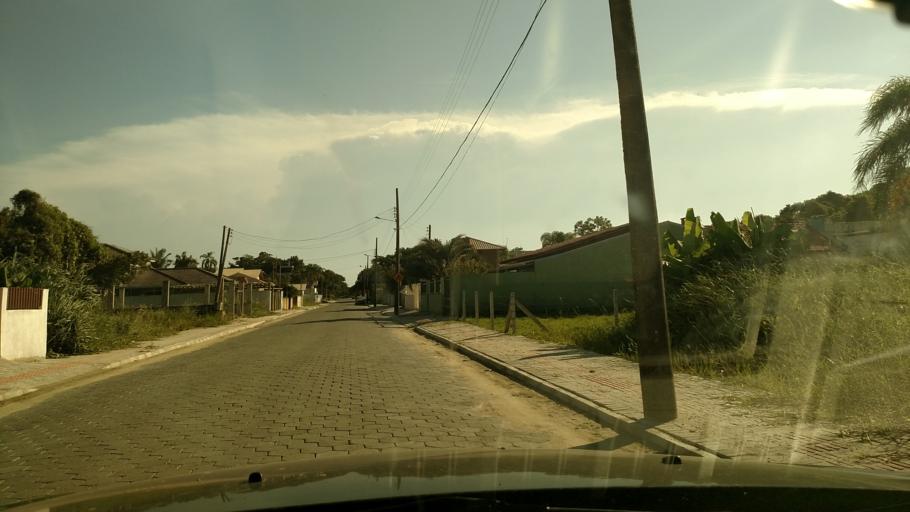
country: BR
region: Santa Catarina
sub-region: Porto Belo
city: Porto Belo
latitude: -27.1787
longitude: -48.5075
